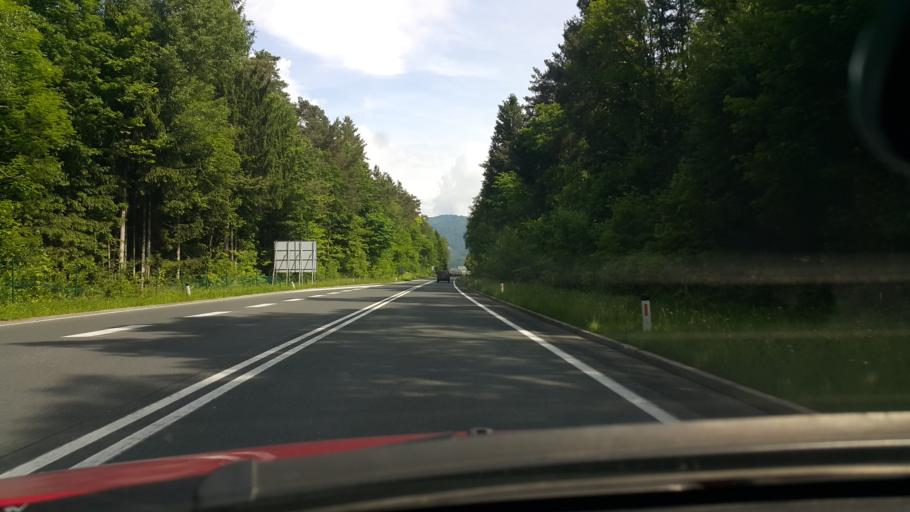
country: SI
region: Trzic
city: Bistrica pri Trzicu
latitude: 46.3186
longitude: 14.2783
